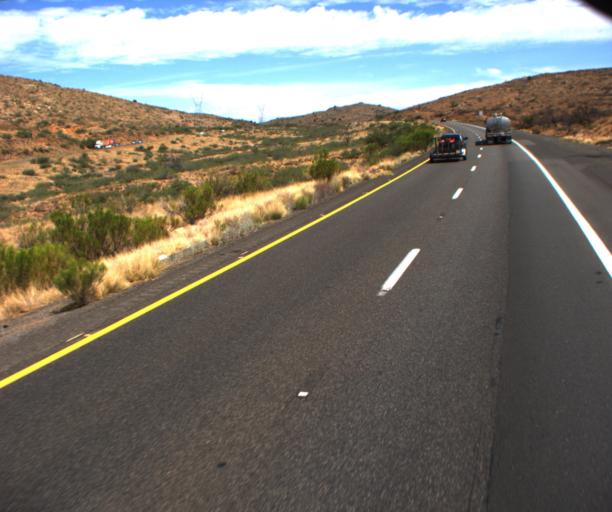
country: US
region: Arizona
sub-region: Yavapai County
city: Cordes Lakes
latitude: 34.2920
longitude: -112.1238
